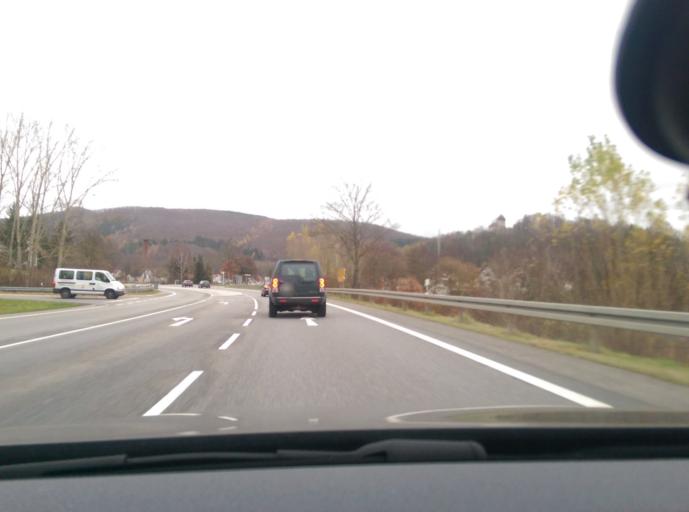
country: DE
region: Hesse
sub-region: Regierungsbezirk Kassel
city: Bad Sooden-Allendorf
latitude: 51.2247
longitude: 9.9874
